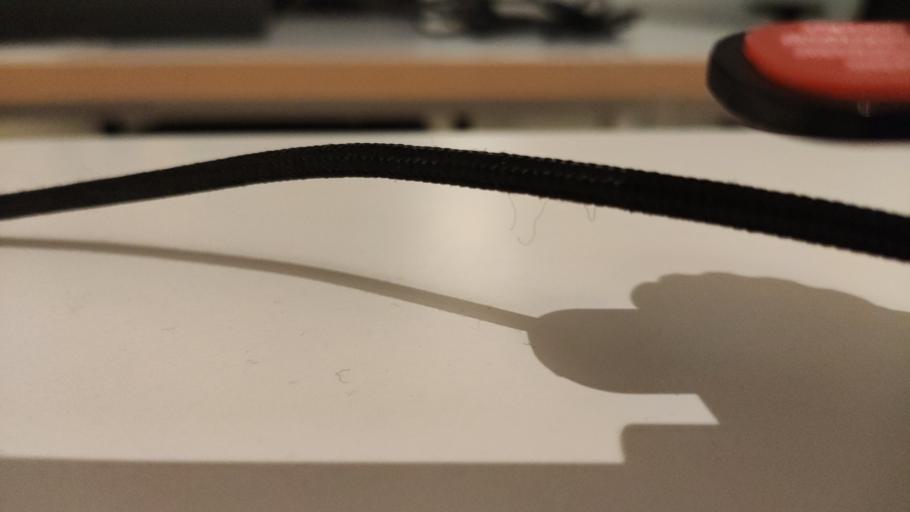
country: RU
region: Moskovskaya
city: Budenovetc
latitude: 56.3903
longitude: 37.6278
